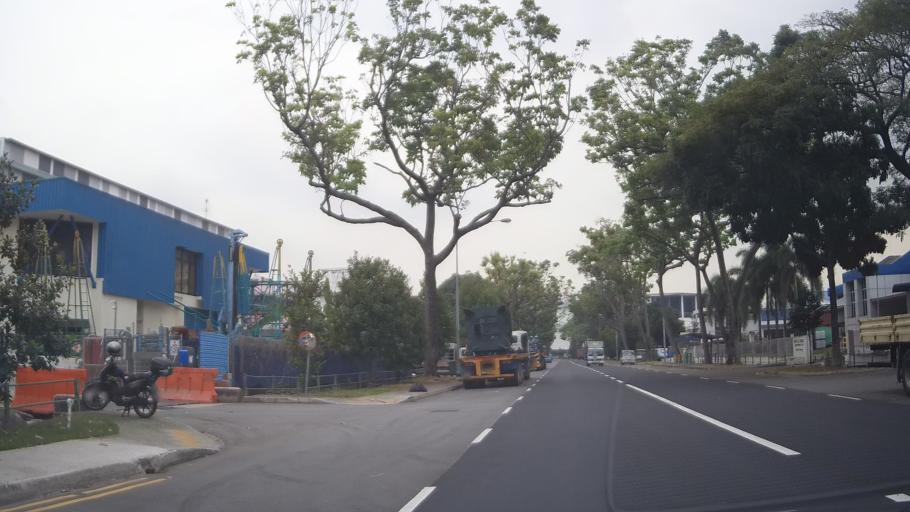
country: MY
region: Johor
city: Johor Bahru
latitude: 1.3149
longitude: 103.6695
